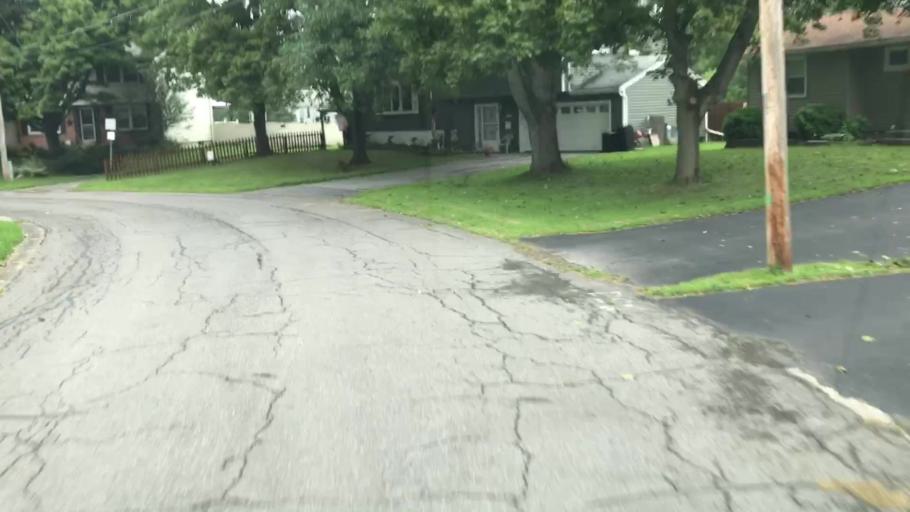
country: US
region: New York
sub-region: Onondaga County
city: Liverpool
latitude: 43.1386
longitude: -76.2191
